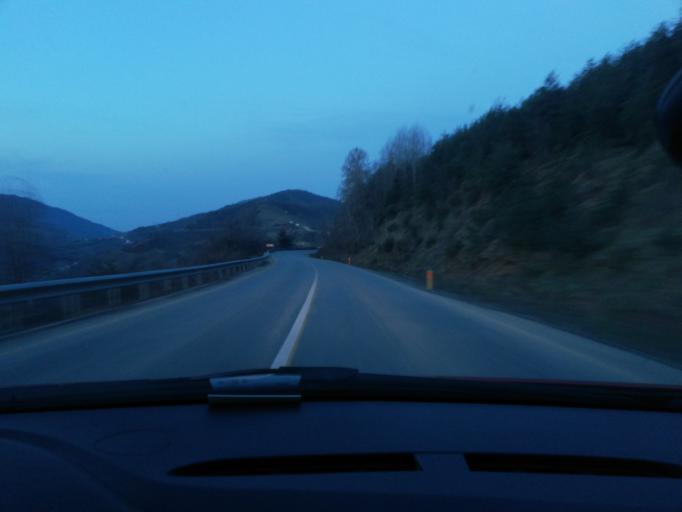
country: TR
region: Kastamonu
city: Inebolu
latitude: 41.9239
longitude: 33.7374
